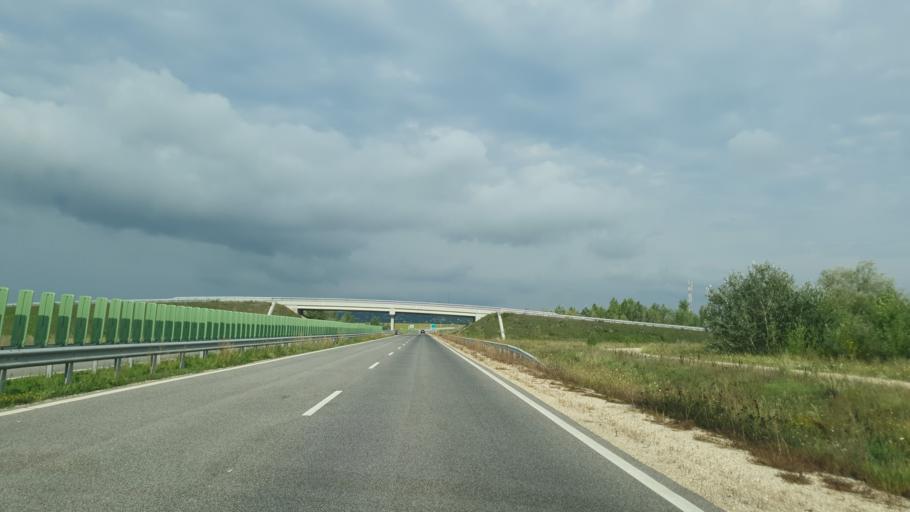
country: HU
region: Fejer
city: Sarszentmihaly
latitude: 47.2087
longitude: 18.3287
